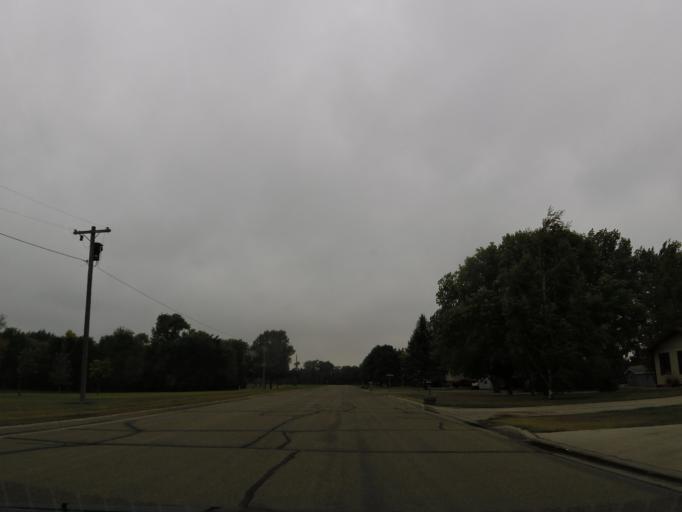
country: US
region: Minnesota
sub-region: Marshall County
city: Warren
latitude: 48.4492
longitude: -96.8847
